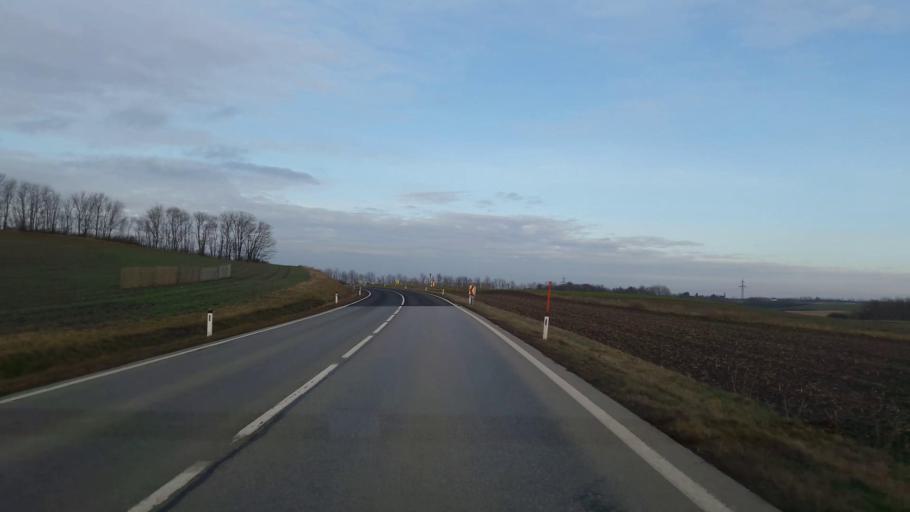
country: AT
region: Lower Austria
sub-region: Politischer Bezirk Mistelbach
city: Staatz
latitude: 48.6855
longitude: 16.4739
